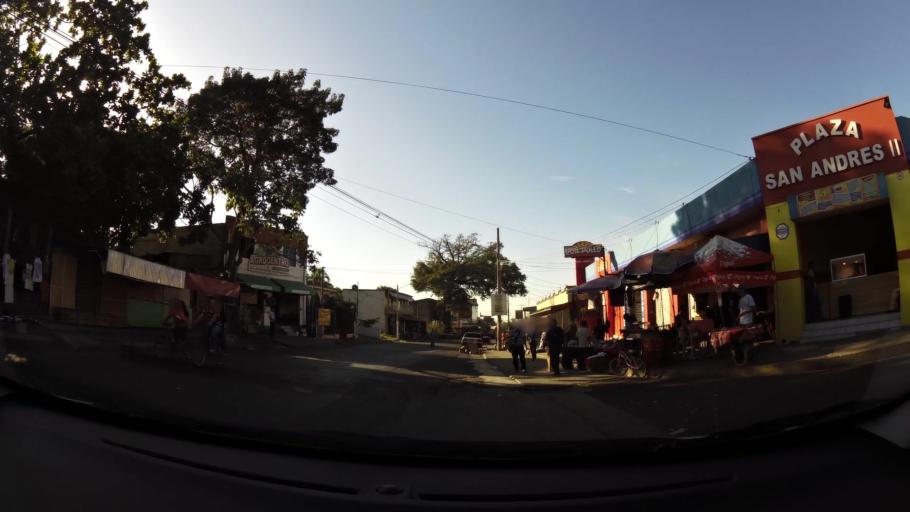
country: SV
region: Sonsonate
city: Sonsonate
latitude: 13.7126
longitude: -89.7175
